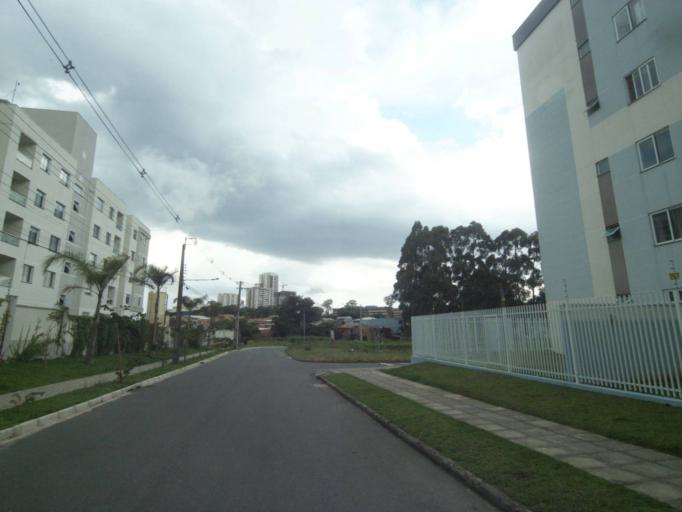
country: BR
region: Parana
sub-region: Curitiba
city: Curitiba
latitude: -25.4422
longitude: -49.3588
